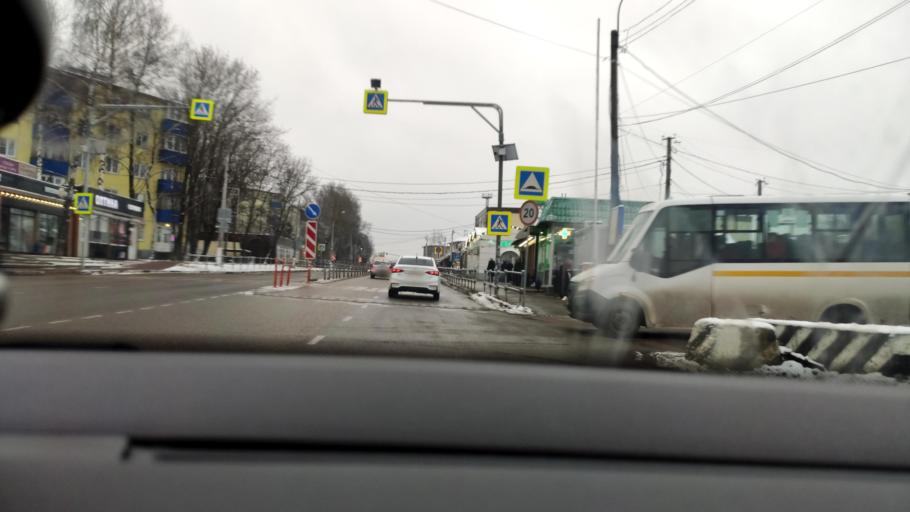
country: RU
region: Moskovskaya
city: Solnechnogorsk
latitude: 56.1864
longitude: 36.9708
